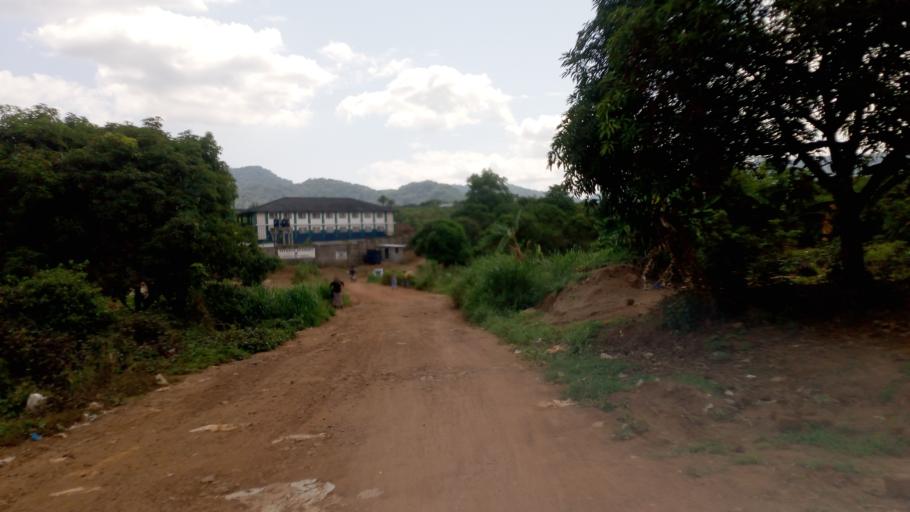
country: SL
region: Western Area
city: Waterloo
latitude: 8.3074
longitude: -13.0809
